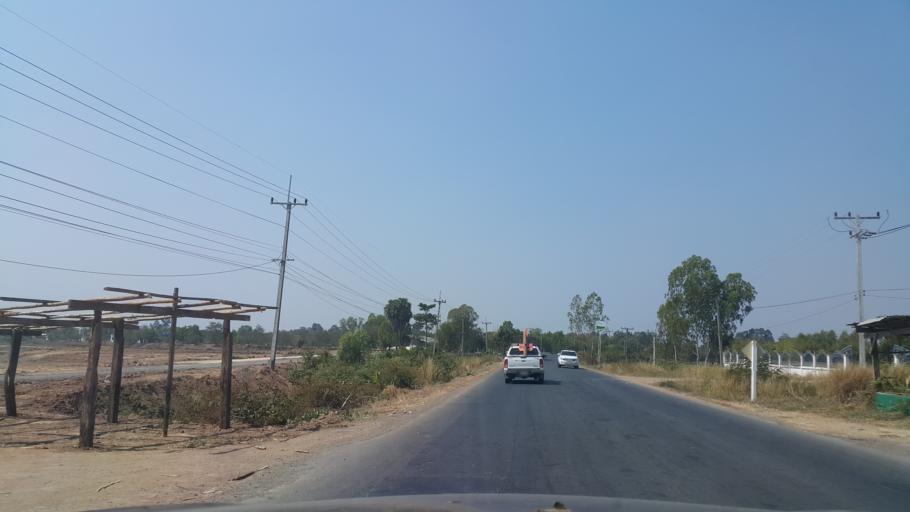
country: TH
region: Buriram
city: Khaen Dong
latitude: 15.2968
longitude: 103.2081
